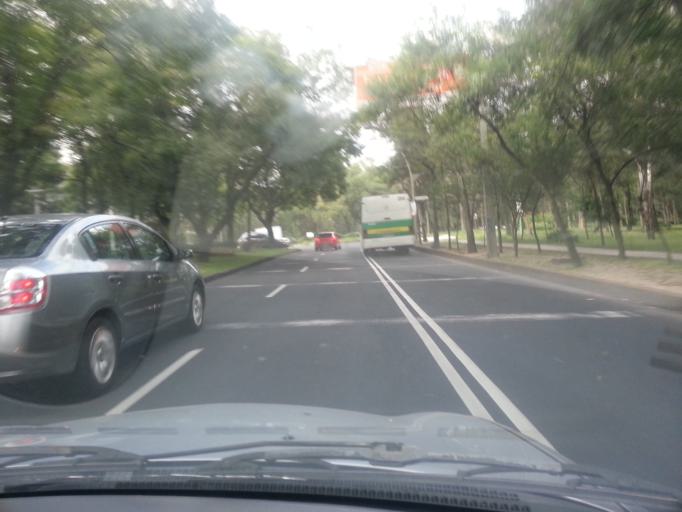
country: MX
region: Mexico City
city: Polanco
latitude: 19.4077
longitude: -99.2236
